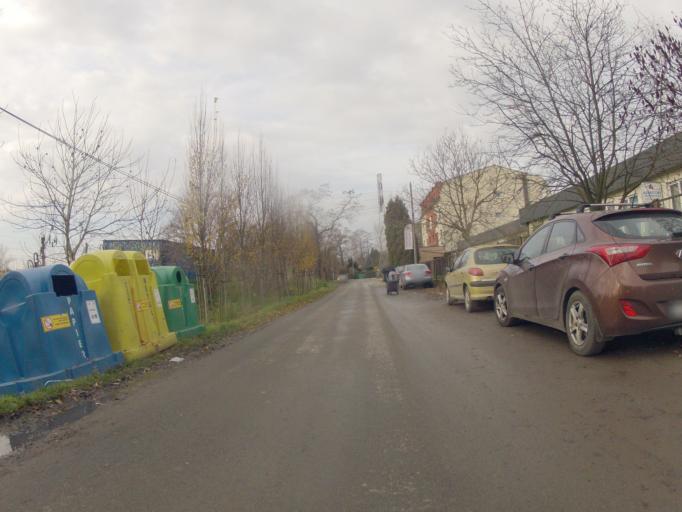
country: PL
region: Lesser Poland Voivodeship
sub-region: Powiat krakowski
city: Rzaska
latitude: 50.0813
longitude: 19.8500
